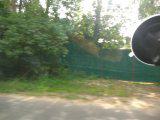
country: RU
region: Moskovskaya
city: Kratovo
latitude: 55.5901
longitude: 38.1508
